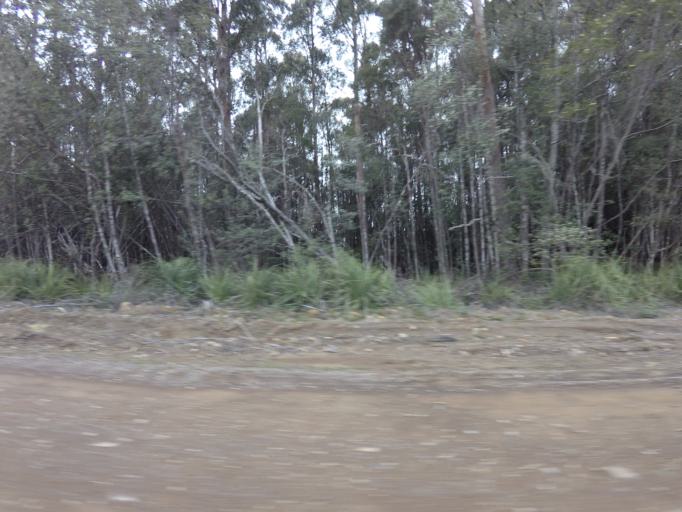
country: AU
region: Tasmania
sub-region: Huon Valley
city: Geeveston
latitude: -43.4896
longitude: 146.8880
